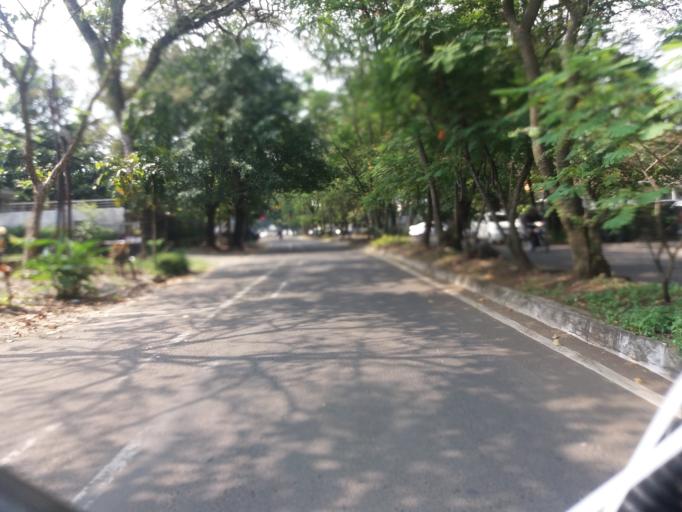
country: ID
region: West Java
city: Bandung
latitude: -6.9058
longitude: 107.6256
